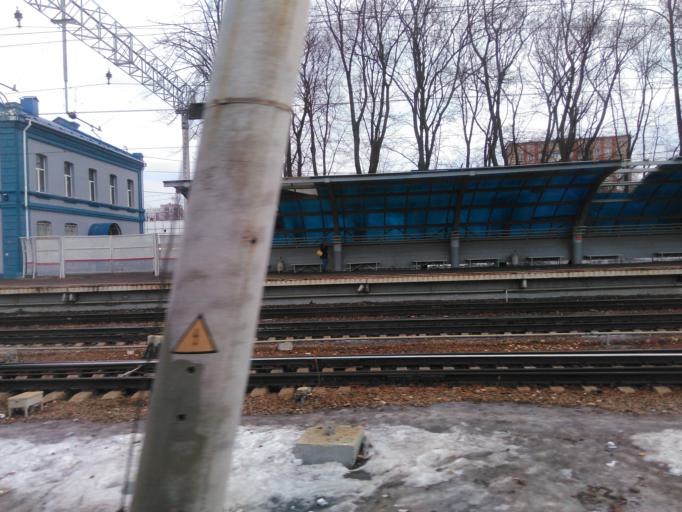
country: RU
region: Moskovskaya
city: Pushkino
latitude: 56.0116
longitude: 37.8390
